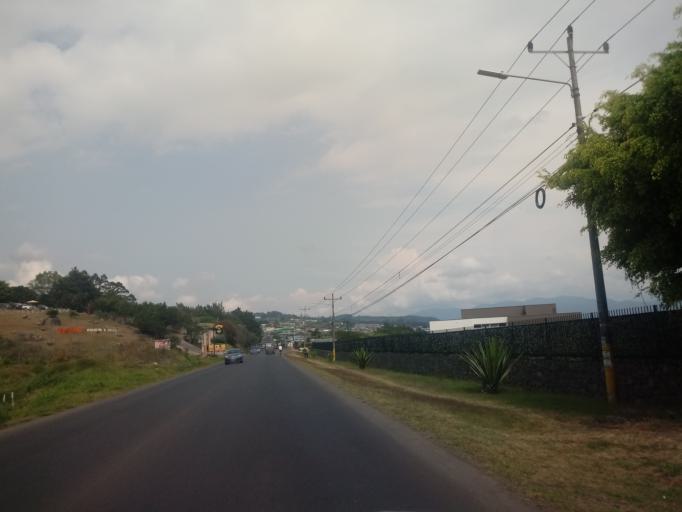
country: CR
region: Cartago
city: Cartago
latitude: 9.8789
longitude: -83.9142
